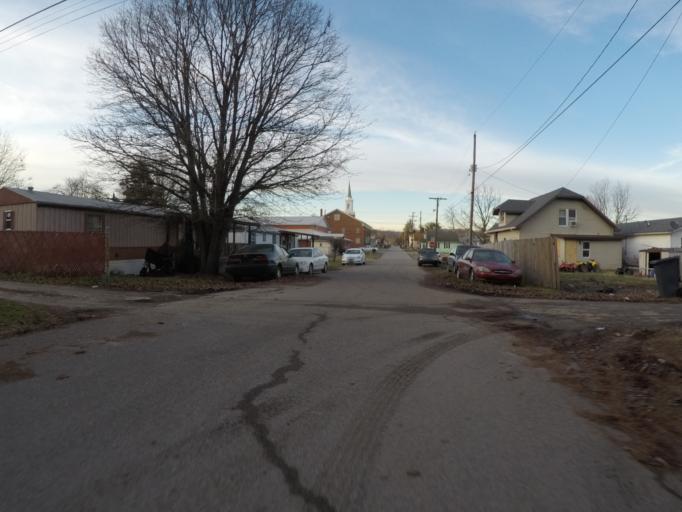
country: US
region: Ohio
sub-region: Lawrence County
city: Burlington
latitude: 38.3990
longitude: -82.5043
